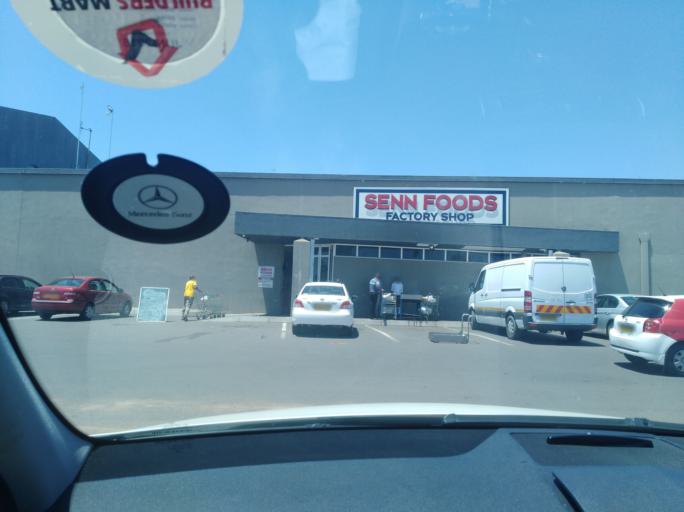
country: BW
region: South East
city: Gaborone
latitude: -24.6797
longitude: 25.9464
